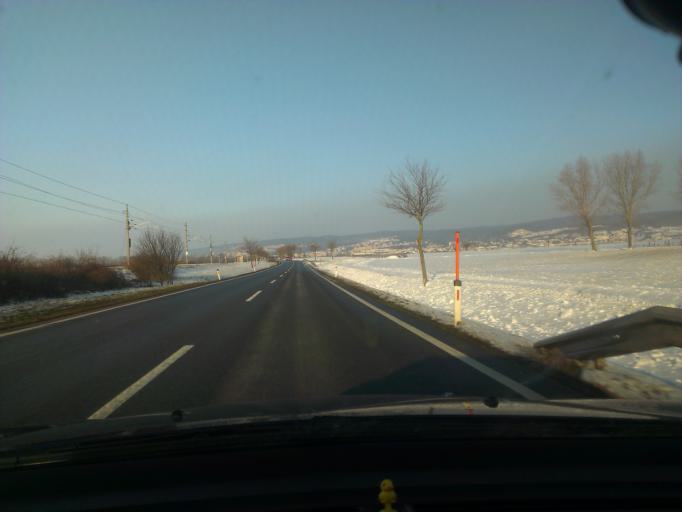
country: AT
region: Burgenland
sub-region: Eisenstadt-Umgebung
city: Trausdorf an der Wulka
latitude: 47.8427
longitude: 16.5705
